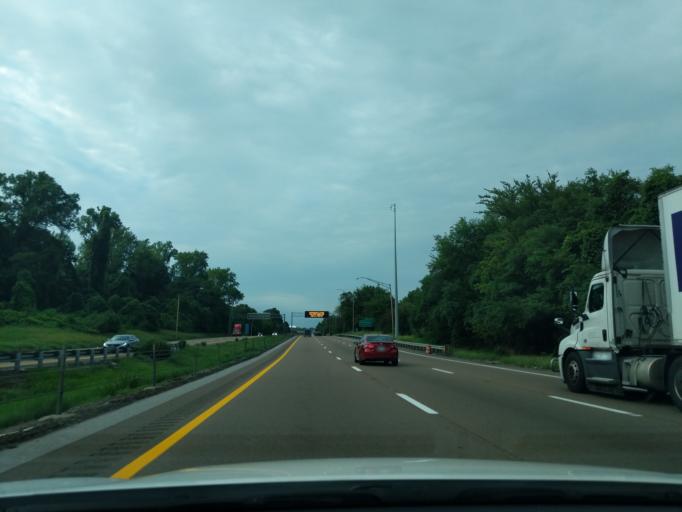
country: US
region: Tennessee
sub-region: Shelby County
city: New South Memphis
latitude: 35.0966
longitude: -90.0764
